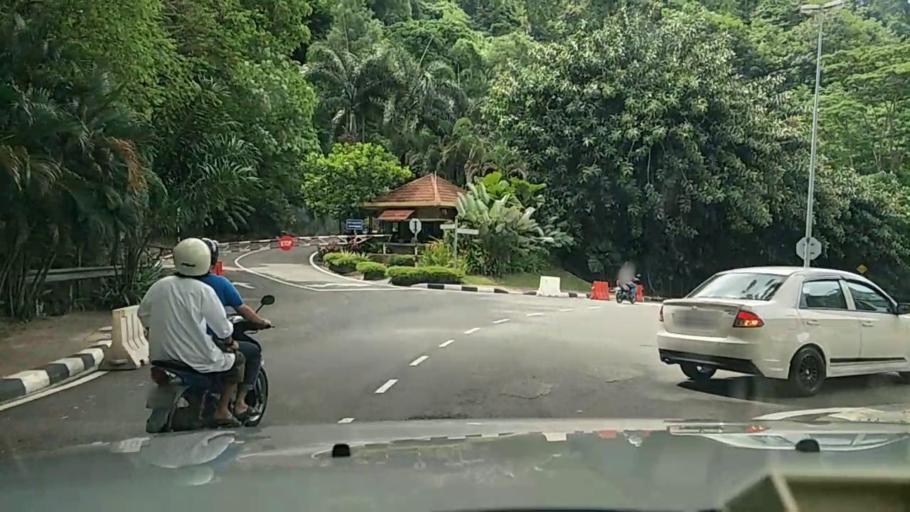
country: MY
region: Selangor
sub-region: Petaling
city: Petaling Jaya
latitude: 3.1668
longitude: 101.6117
